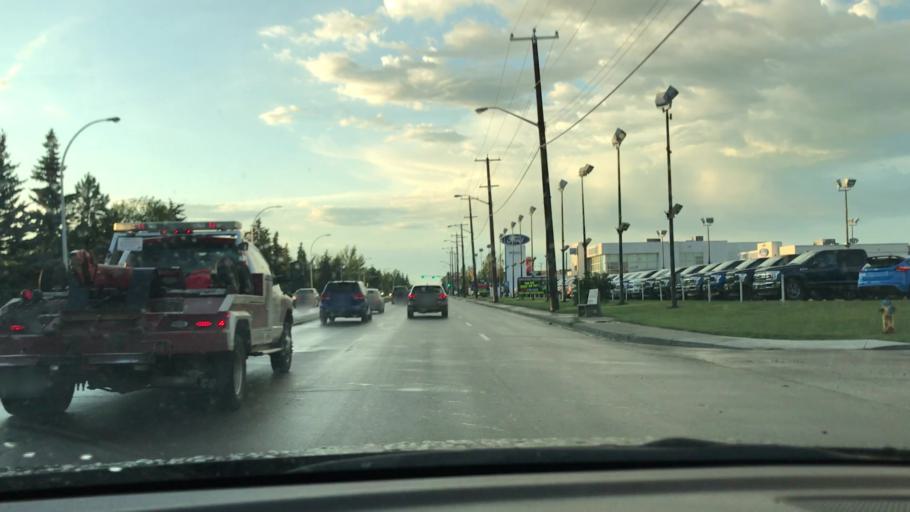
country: CA
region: Alberta
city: Edmonton
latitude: 53.5098
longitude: -113.4428
